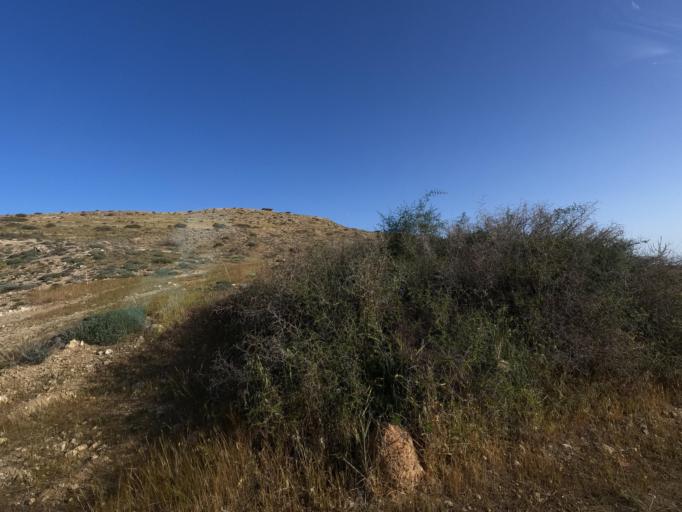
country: CY
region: Lefkosia
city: Astromeritis
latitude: 35.0789
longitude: 33.0260
